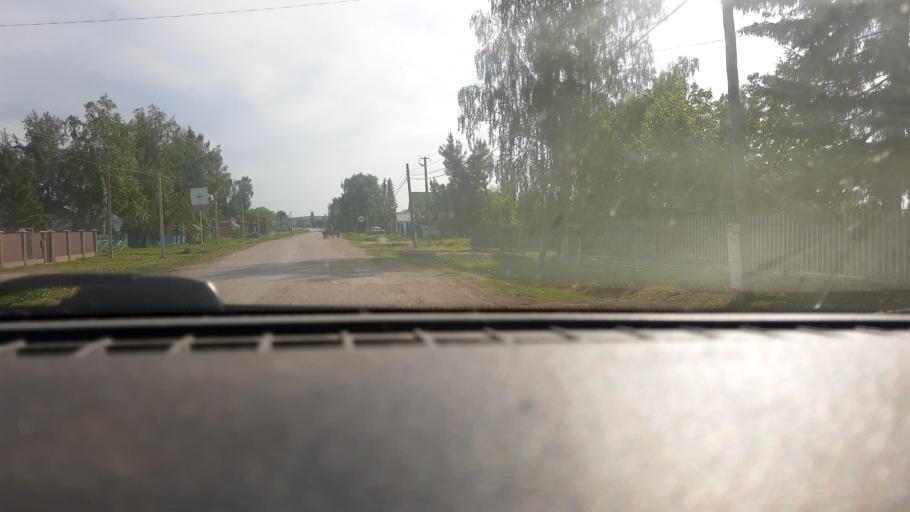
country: RU
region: Bashkortostan
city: Iglino
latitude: 54.7169
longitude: 56.4104
